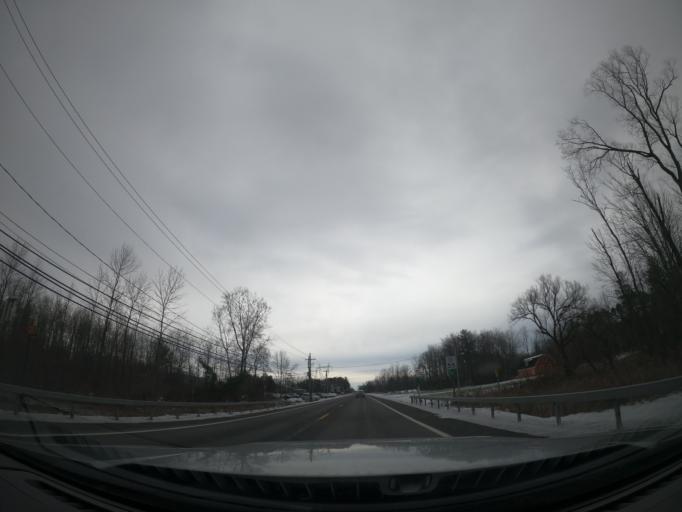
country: US
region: New York
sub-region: Madison County
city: Bridgeport
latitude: 43.1550
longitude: -75.9564
